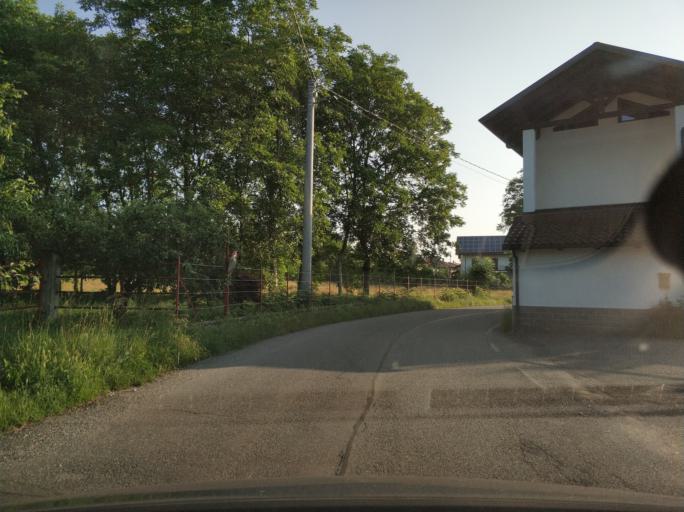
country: IT
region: Piedmont
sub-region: Provincia di Torino
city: Cafasse
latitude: 45.2379
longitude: 7.5250
